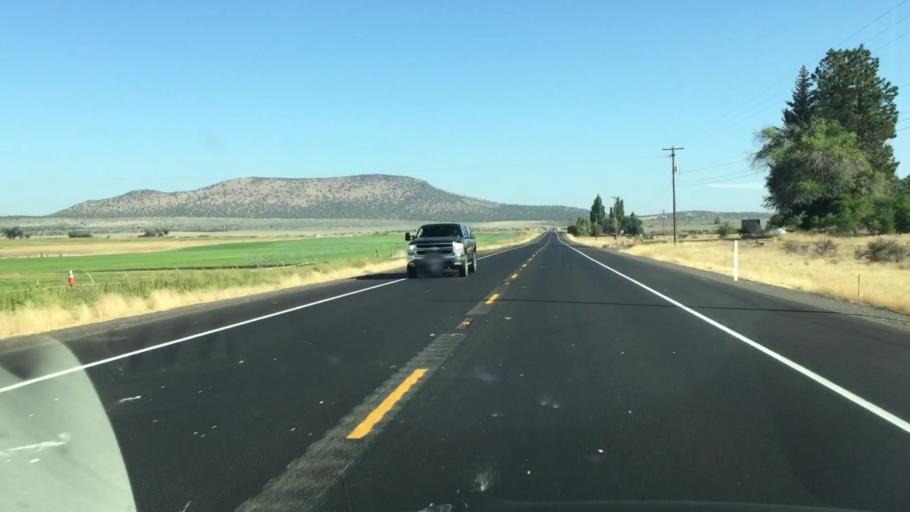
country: US
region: Oregon
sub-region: Deschutes County
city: Terrebonne
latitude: 44.4383
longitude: -121.1991
